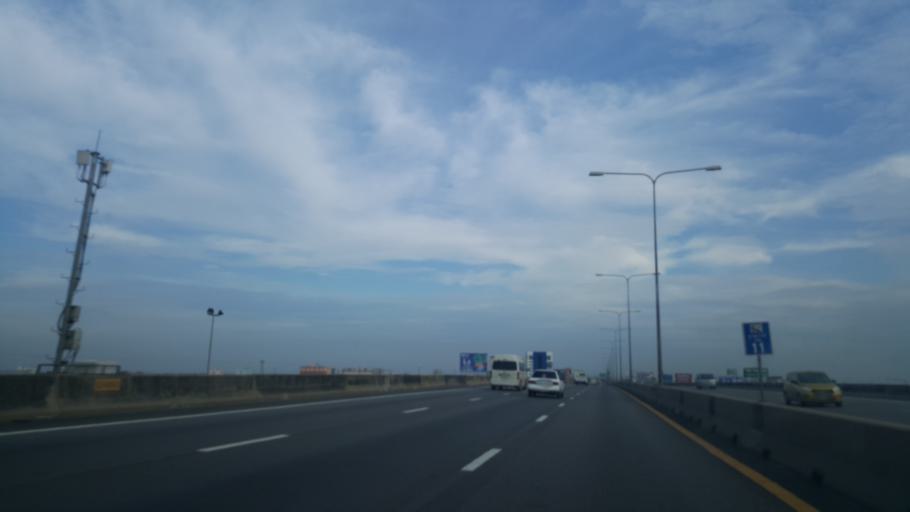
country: TH
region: Bangkok
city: Bang Na
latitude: 13.6395
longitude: 100.7012
